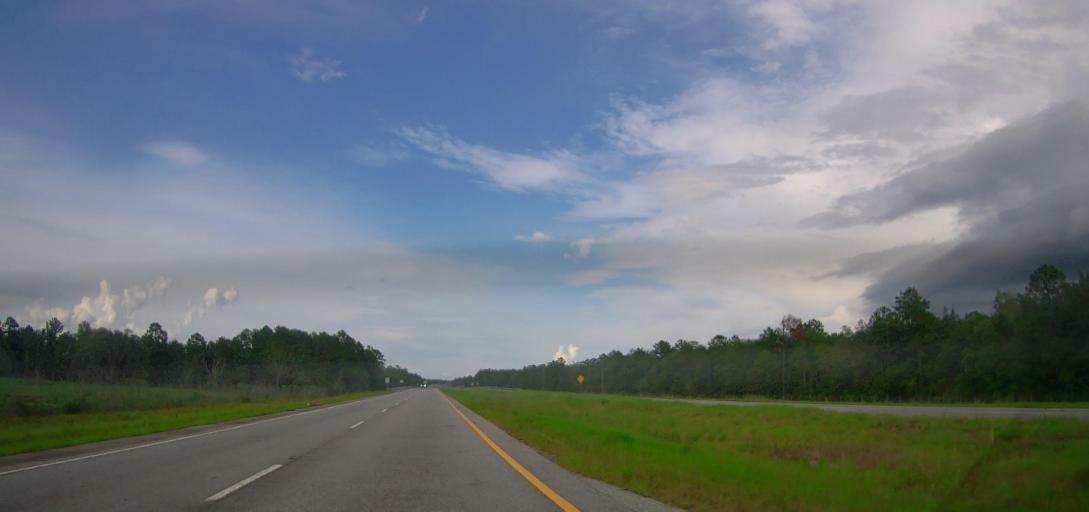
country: US
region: Georgia
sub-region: Pierce County
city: Blackshear
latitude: 31.4498
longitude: -82.0650
